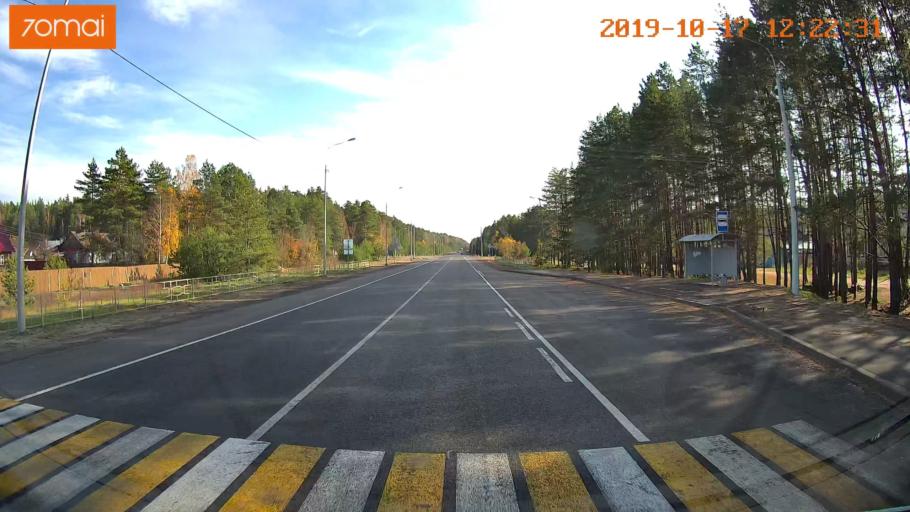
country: RU
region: Rjazan
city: Gus'-Zheleznyy
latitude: 55.0515
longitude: 41.1733
